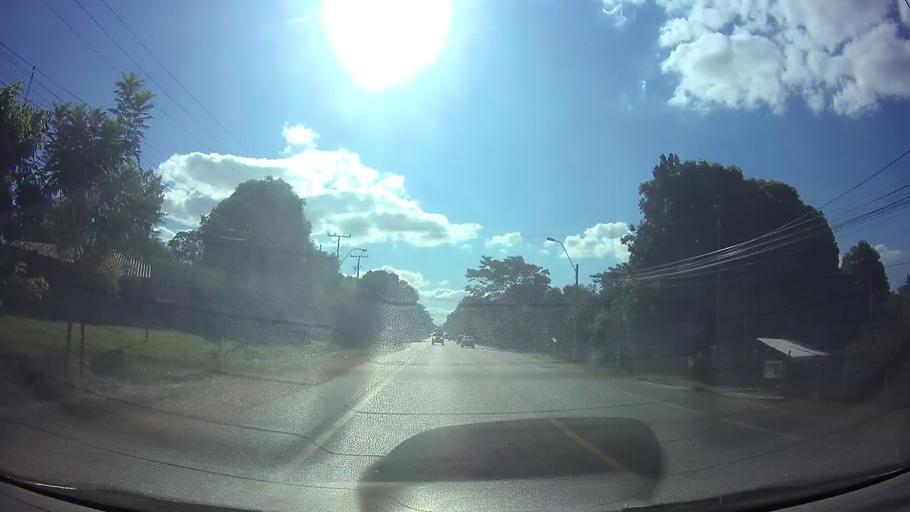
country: PY
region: Cordillera
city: Caacupe
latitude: -25.3895
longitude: -57.1628
